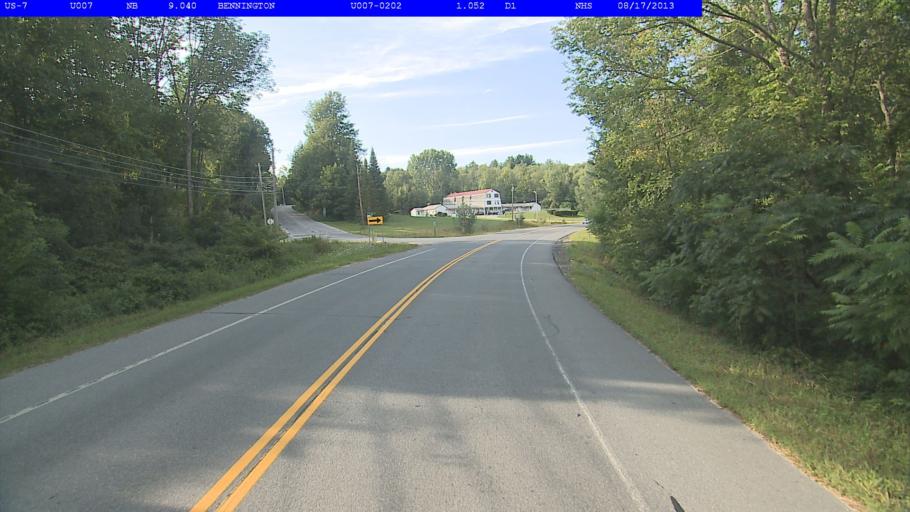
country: US
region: Vermont
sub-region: Bennington County
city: Bennington
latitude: 42.8522
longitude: -73.2040
